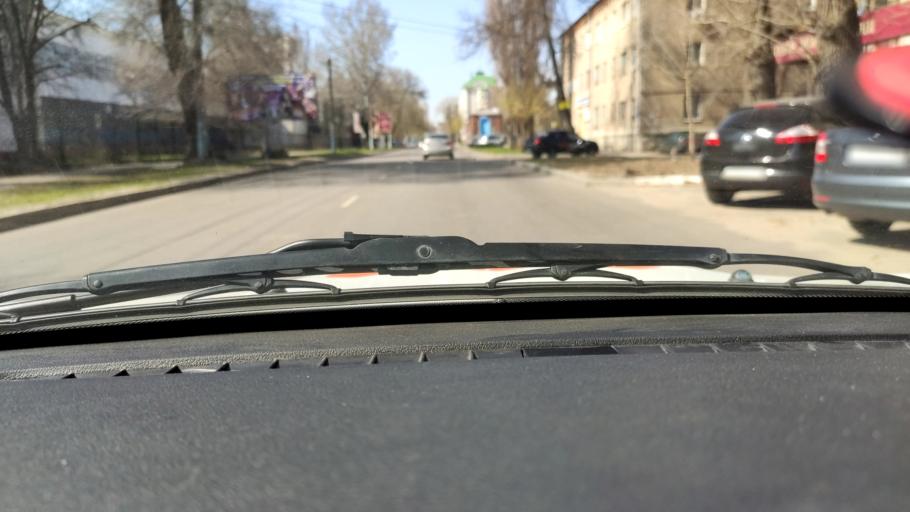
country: RU
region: Voronezj
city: Voronezh
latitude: 51.6824
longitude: 39.2027
